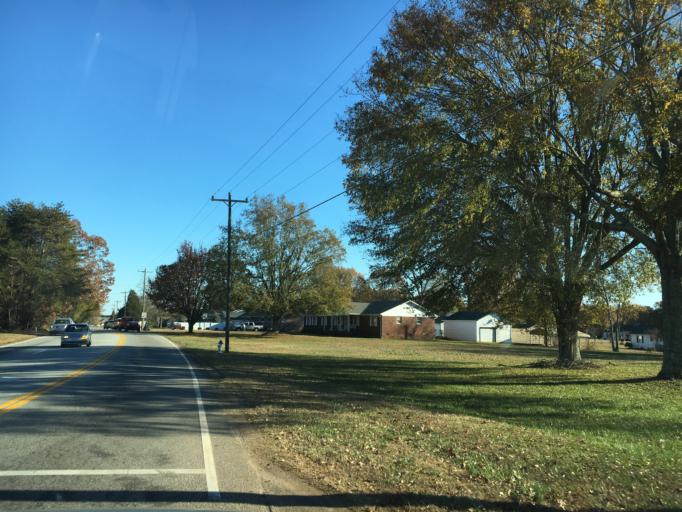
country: US
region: South Carolina
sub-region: Spartanburg County
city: Duncan
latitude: 34.9754
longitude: -82.1589
